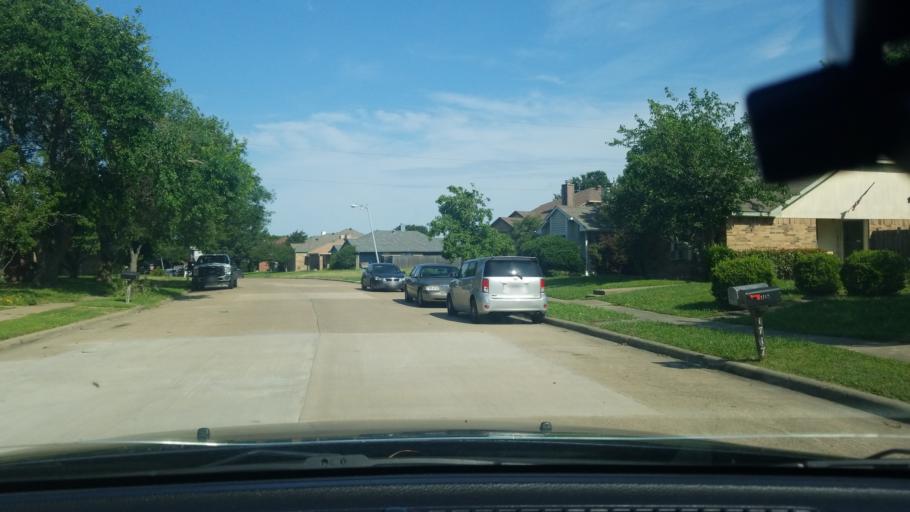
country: US
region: Texas
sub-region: Dallas County
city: Sunnyvale
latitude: 32.7783
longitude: -96.5723
